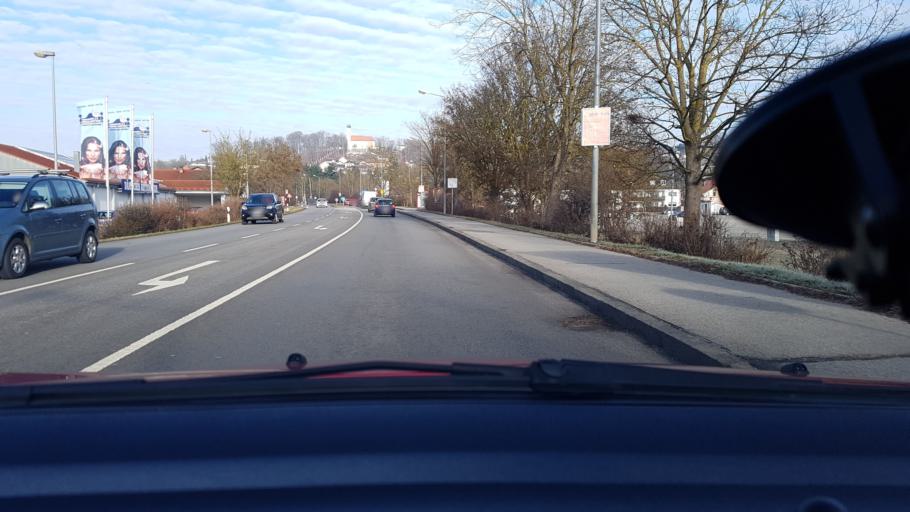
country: DE
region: Bavaria
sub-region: Lower Bavaria
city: Pfarrkirchen
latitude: 48.4271
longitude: 12.9432
